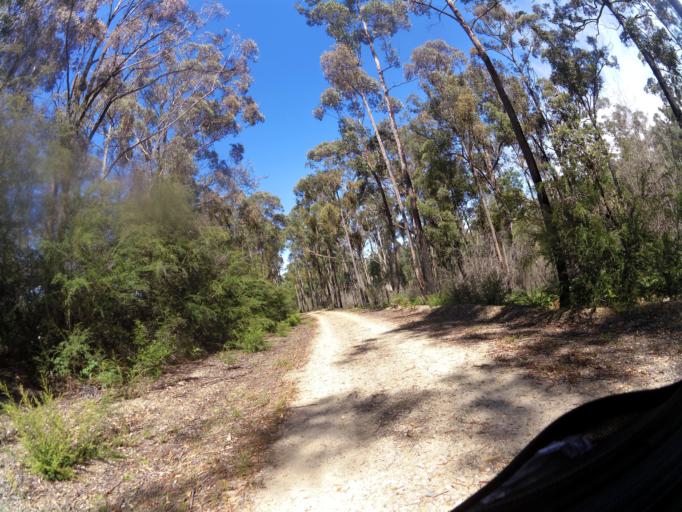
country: AU
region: Victoria
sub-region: East Gippsland
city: Lakes Entrance
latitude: -37.7189
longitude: 148.1236
